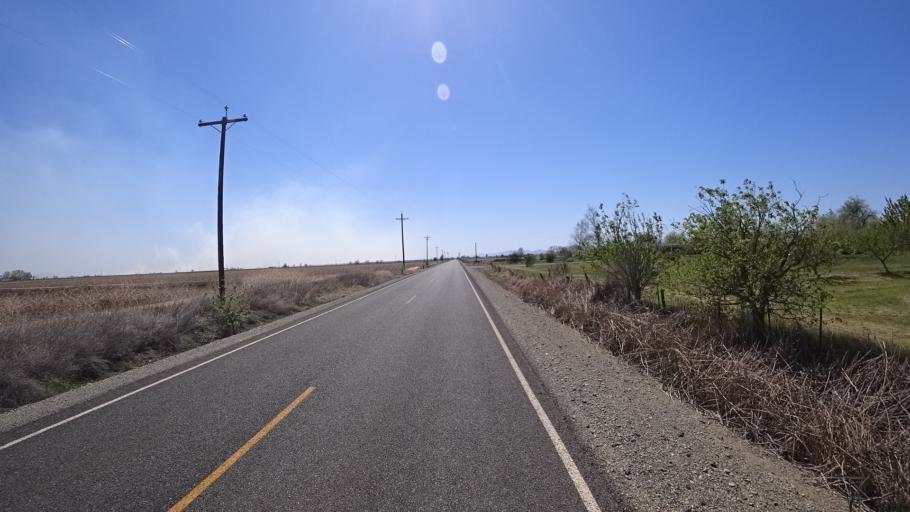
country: US
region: California
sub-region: Glenn County
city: Willows
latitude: 39.4112
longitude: -122.2485
